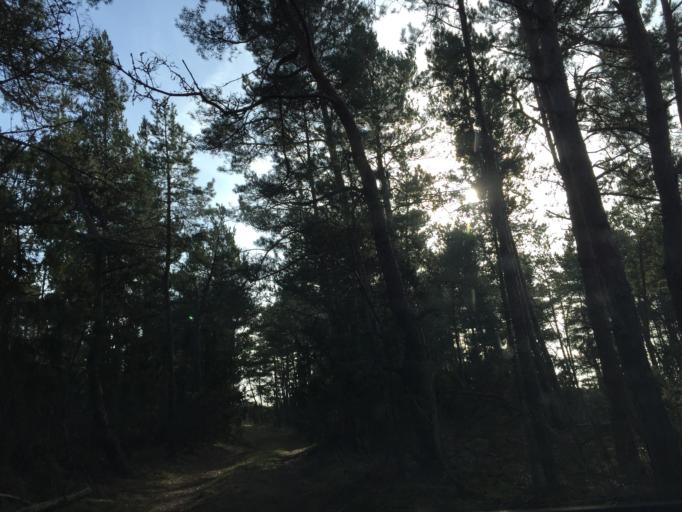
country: EE
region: Saare
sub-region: Kuressaare linn
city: Kuressaare
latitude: 58.3767
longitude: 21.9985
